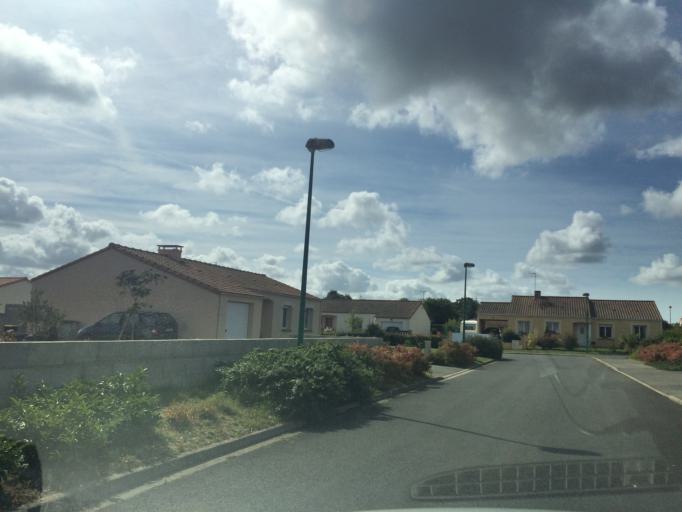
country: FR
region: Pays de la Loire
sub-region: Departement de la Loire-Atlantique
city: Chemere
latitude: 47.1147
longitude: -1.9187
